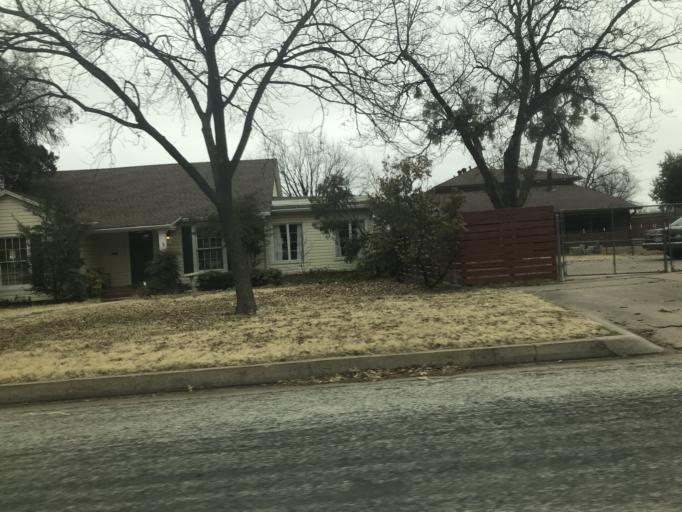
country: US
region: Texas
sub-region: Taylor County
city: Abilene
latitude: 32.4377
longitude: -99.7468
